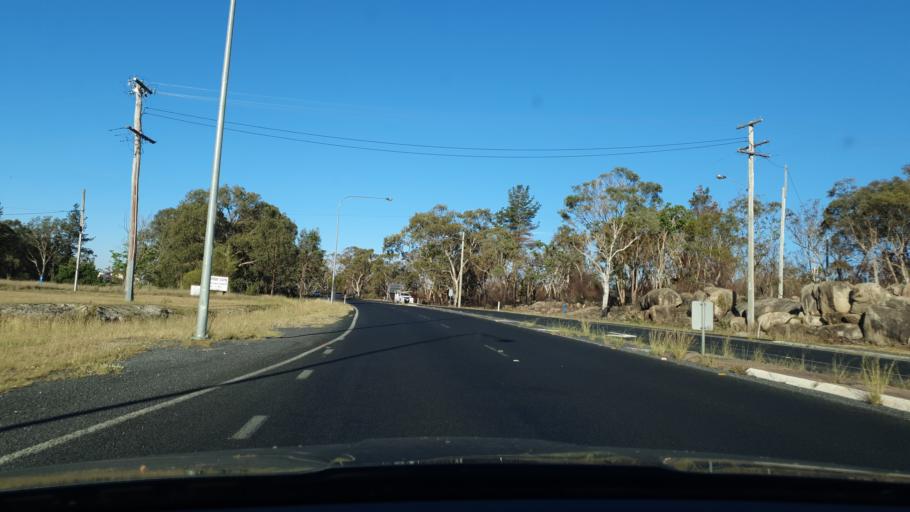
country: AU
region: Queensland
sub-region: Southern Downs
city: Stanthorpe
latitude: -28.6356
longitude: 151.9509
